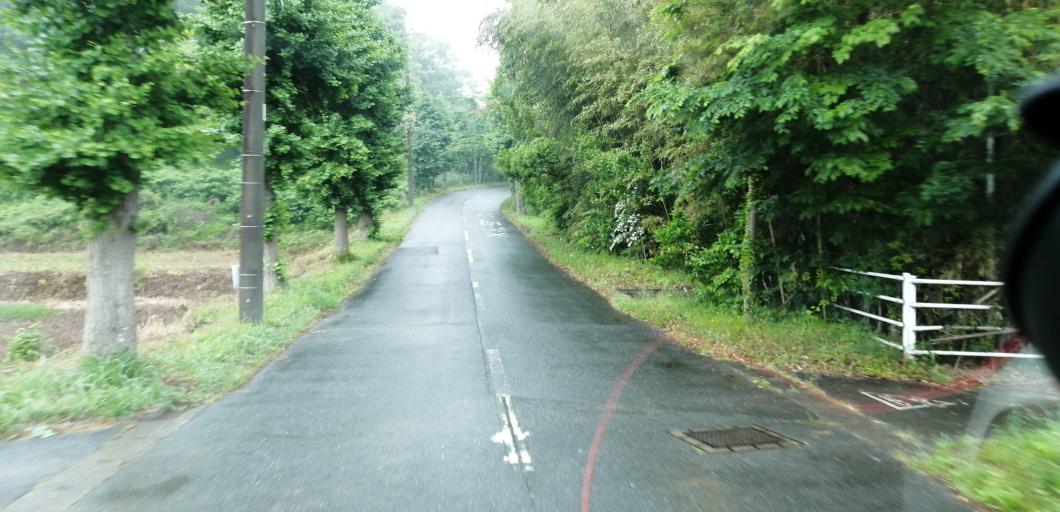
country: JP
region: Chiba
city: Ichihara
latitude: 35.4620
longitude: 140.1092
